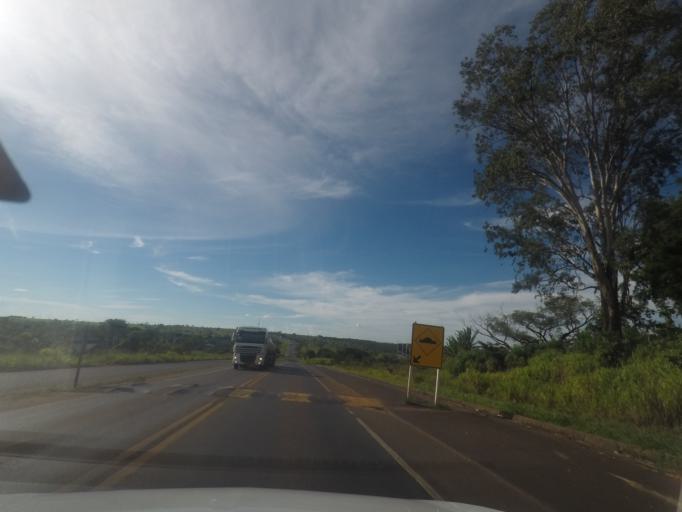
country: BR
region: Minas Gerais
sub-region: Monte Alegre De Minas
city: Monte Alegre de Minas
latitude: -18.8837
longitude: -49.0539
